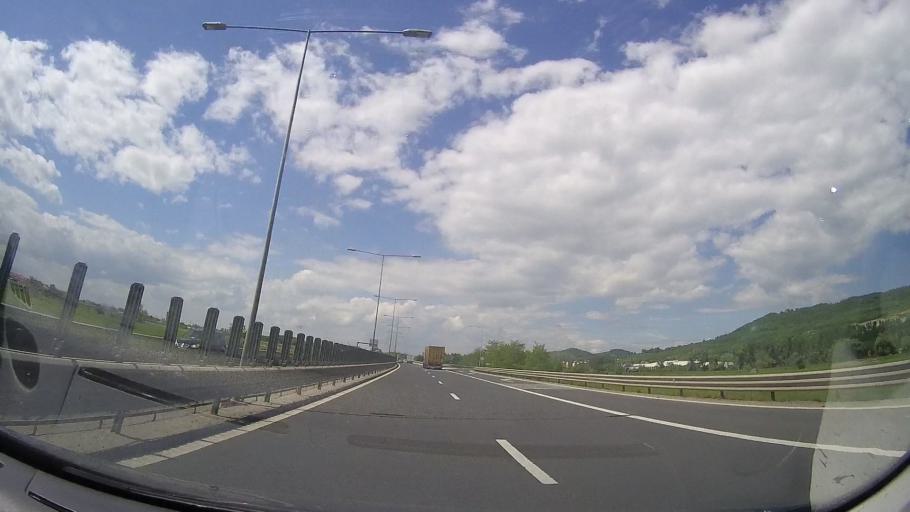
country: RO
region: Sibiu
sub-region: Comuna Selimbar
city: Selimbar
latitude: 45.7969
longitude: 24.1936
